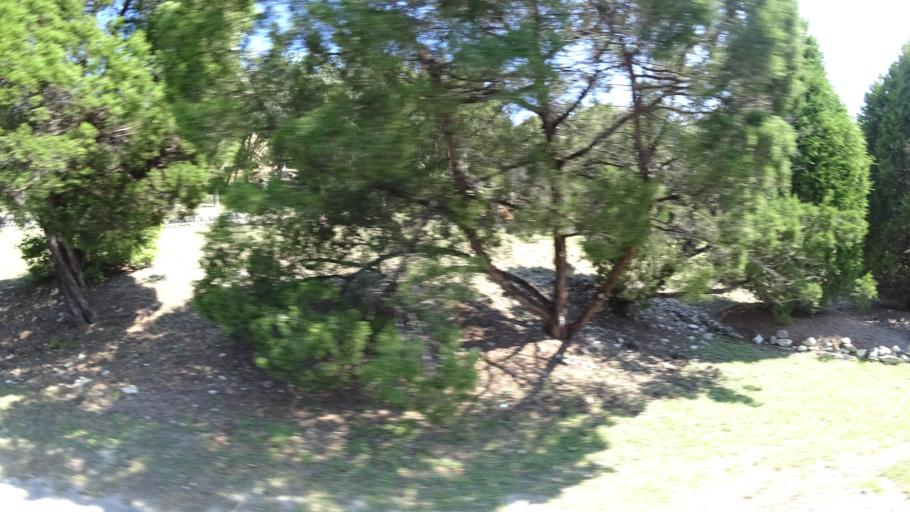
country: US
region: Texas
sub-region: Travis County
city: West Lake Hills
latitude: 30.3052
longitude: -97.7952
